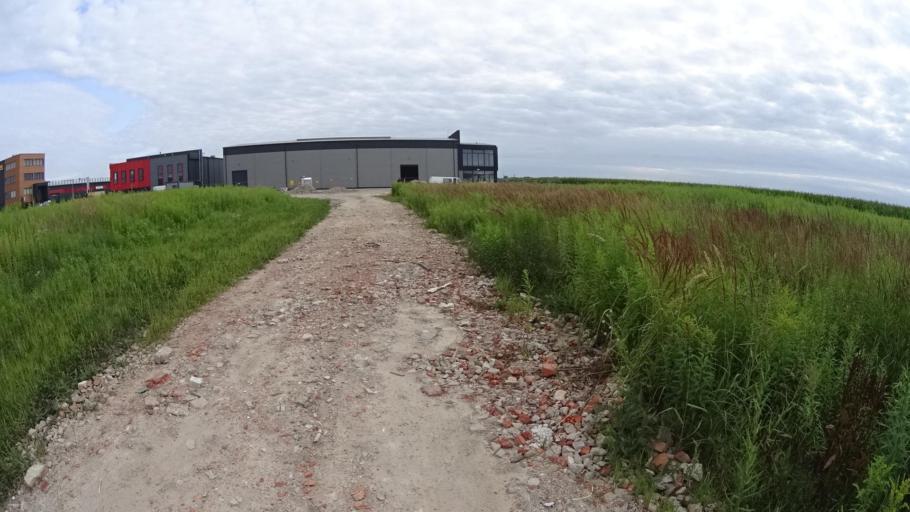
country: PL
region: Masovian Voivodeship
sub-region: Warszawa
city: Bemowo
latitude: 52.2356
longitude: 20.8809
